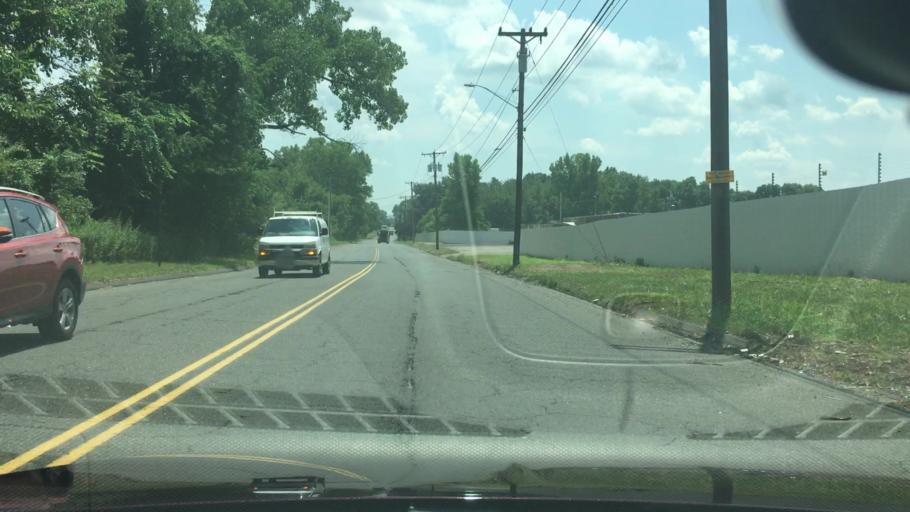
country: US
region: Connecticut
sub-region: Hartford County
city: Kensington
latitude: 41.6457
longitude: -72.7511
